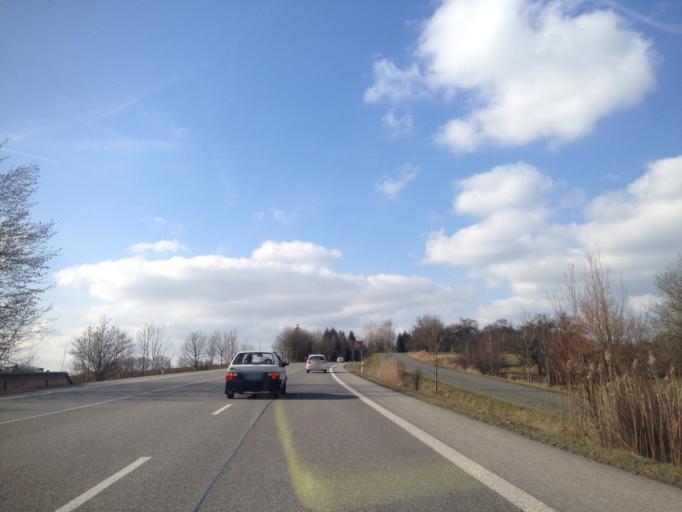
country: CZ
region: Kralovehradecky
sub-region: Okres Jicin
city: Sobotka
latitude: 50.4564
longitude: 15.2206
